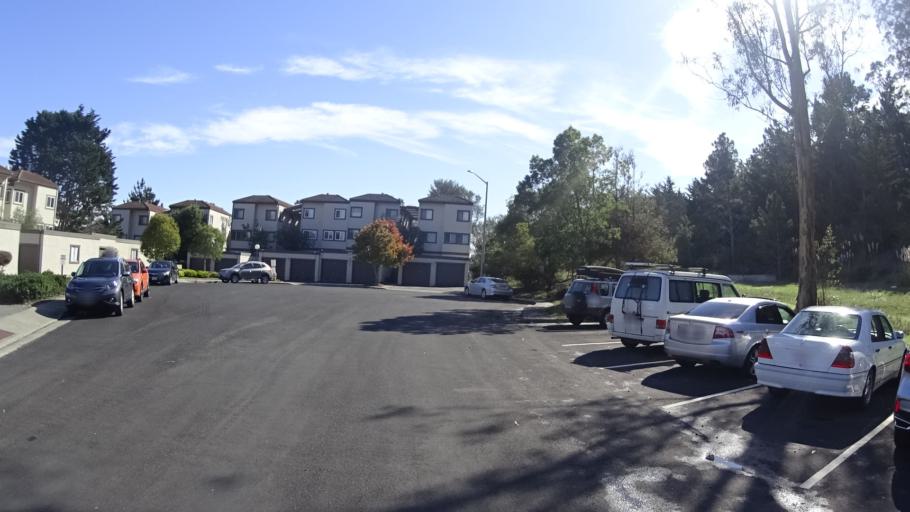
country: US
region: California
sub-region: San Mateo County
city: Pacifica
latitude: 37.6414
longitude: -122.4651
